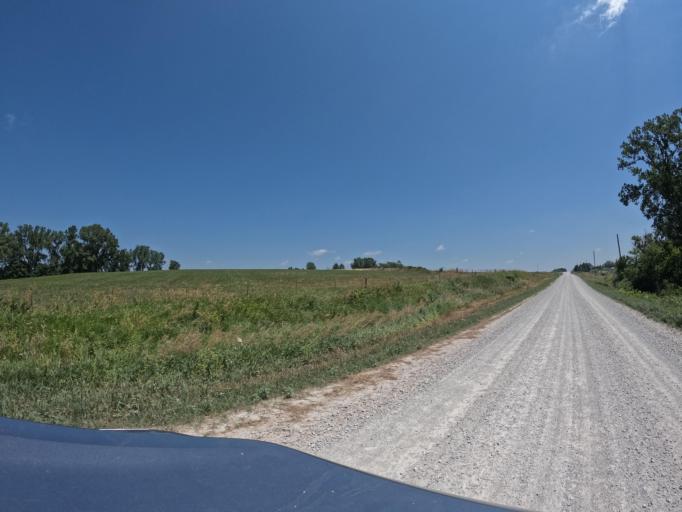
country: US
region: Iowa
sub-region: Keokuk County
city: Sigourney
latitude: 41.2579
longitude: -92.1736
